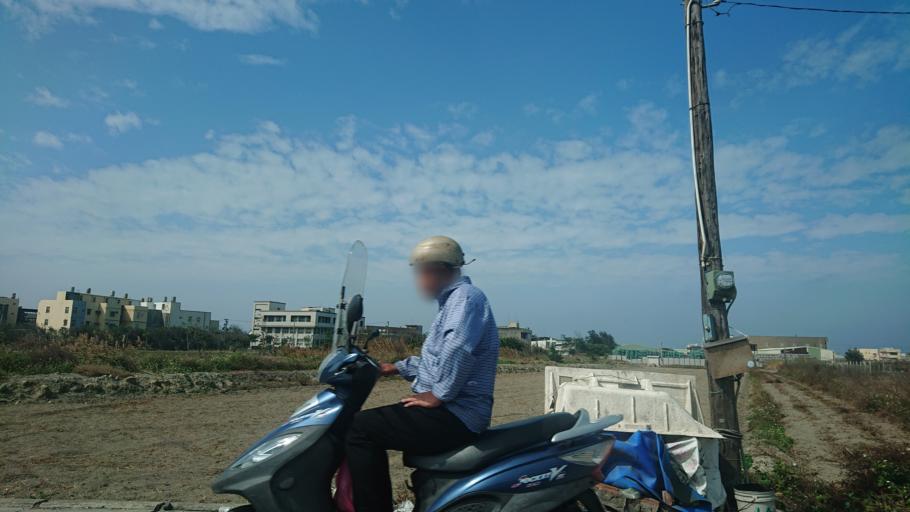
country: TW
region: Taiwan
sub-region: Changhua
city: Chang-hua
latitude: 23.9251
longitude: 120.3227
